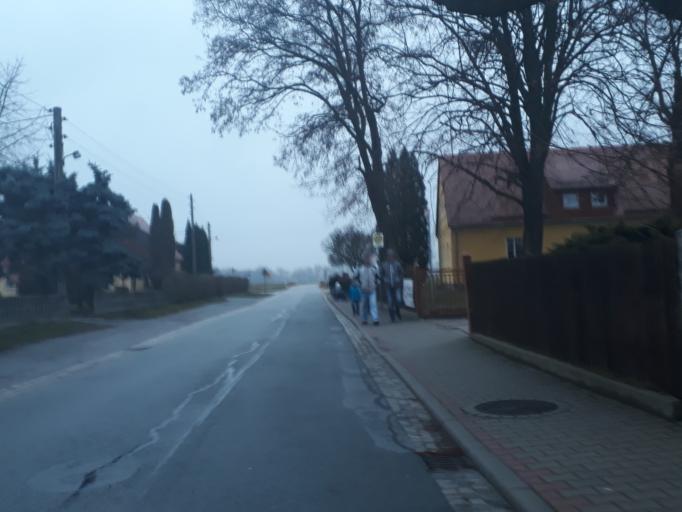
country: DE
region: Saxony
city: Guttau
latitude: 51.2607
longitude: 14.5603
